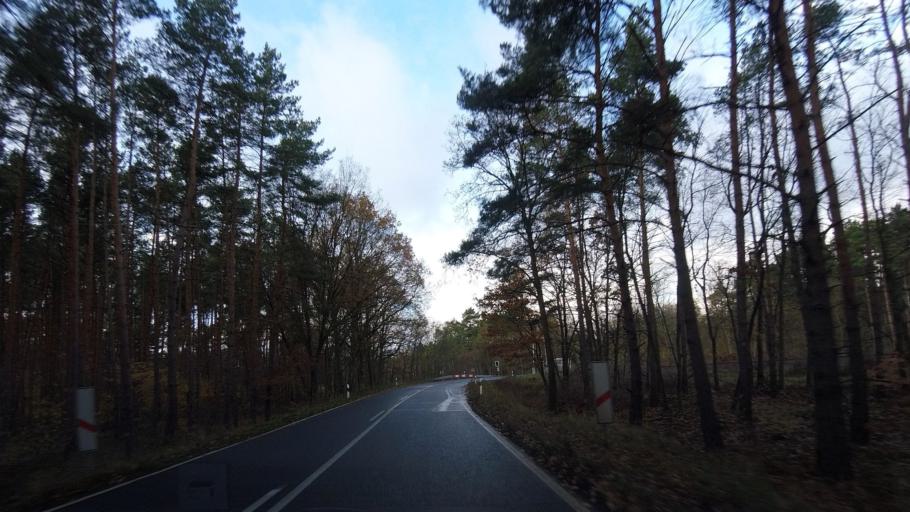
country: DE
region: Brandenburg
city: Niedergorsdorf
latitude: 52.0328
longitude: 12.9460
